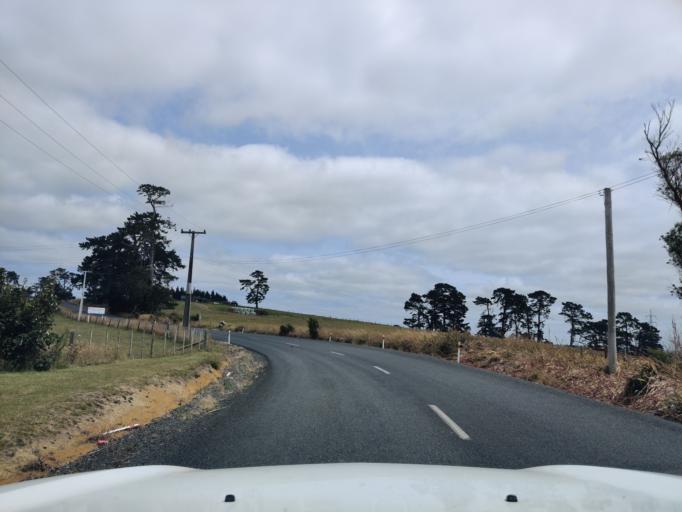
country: NZ
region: Waikato
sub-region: Waikato District
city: Te Kauwhata
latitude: -37.5139
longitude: 175.1758
